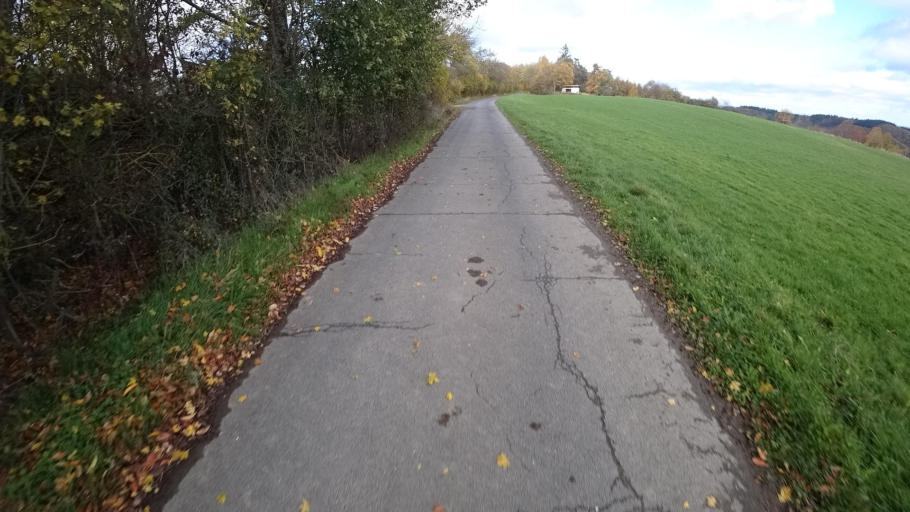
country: DE
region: Rheinland-Pfalz
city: Lind
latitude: 50.4892
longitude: 6.9354
